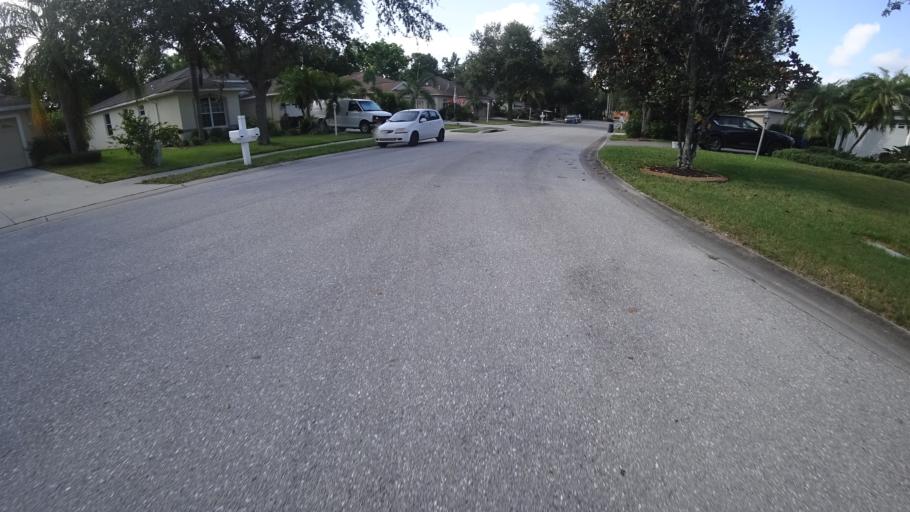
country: US
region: Florida
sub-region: Sarasota County
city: North Sarasota
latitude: 27.3936
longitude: -82.5041
